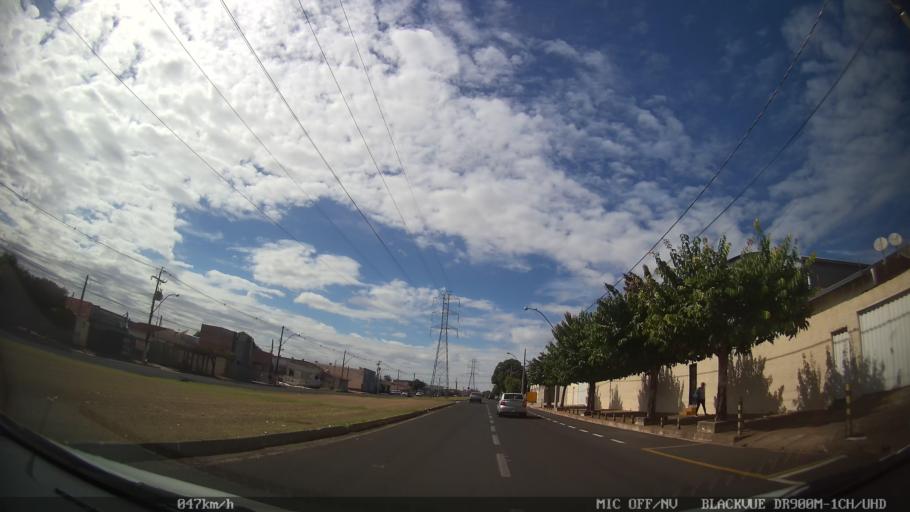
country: BR
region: Sao Paulo
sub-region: Bady Bassitt
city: Bady Bassitt
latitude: -20.8120
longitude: -49.5135
